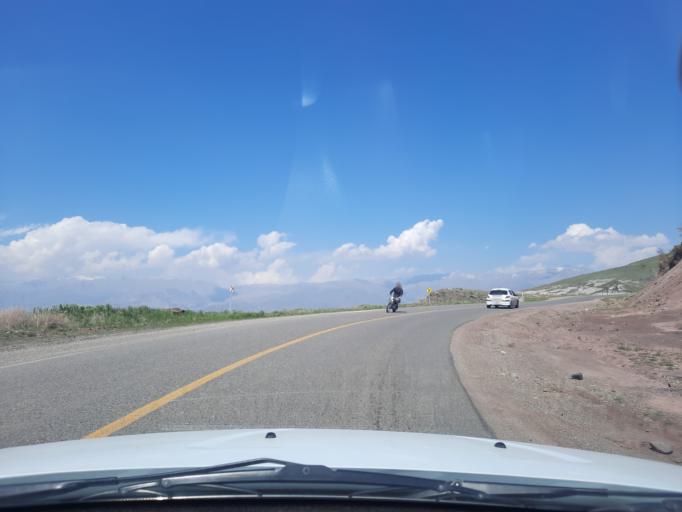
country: IR
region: Qazvin
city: Qazvin
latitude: 36.4067
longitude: 50.2301
